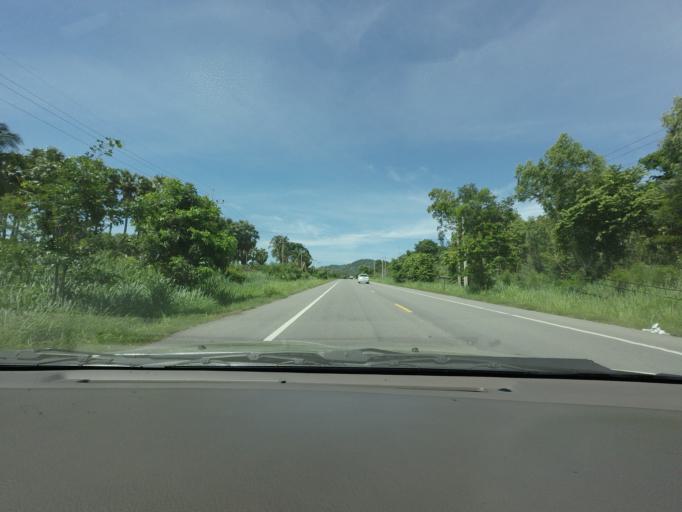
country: TH
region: Chon Buri
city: Si Racha
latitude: 13.2519
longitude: 100.9609
